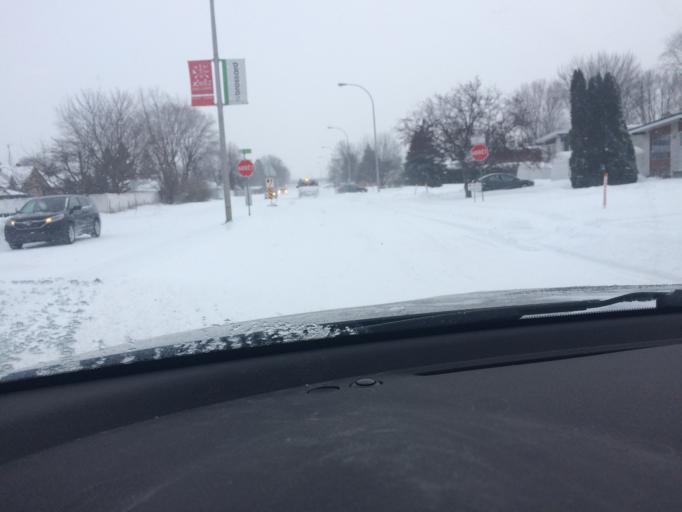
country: CA
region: Quebec
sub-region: Monteregie
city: Brossard
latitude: 45.4671
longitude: -73.4612
